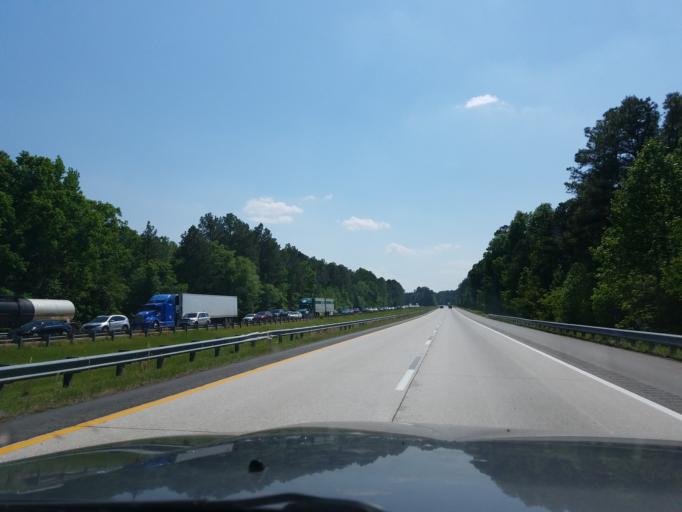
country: US
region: North Carolina
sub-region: Granville County
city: Creedmoor
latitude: 36.2147
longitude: -78.6689
